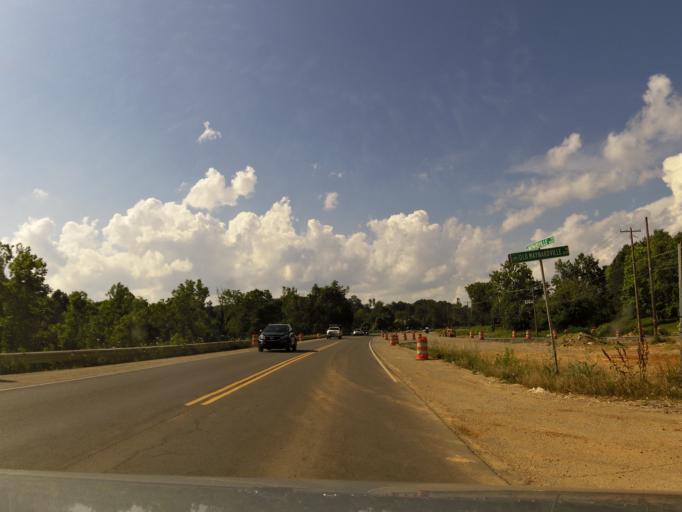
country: US
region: Tennessee
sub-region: Union County
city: Condon
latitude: 36.1197
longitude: -83.9148
